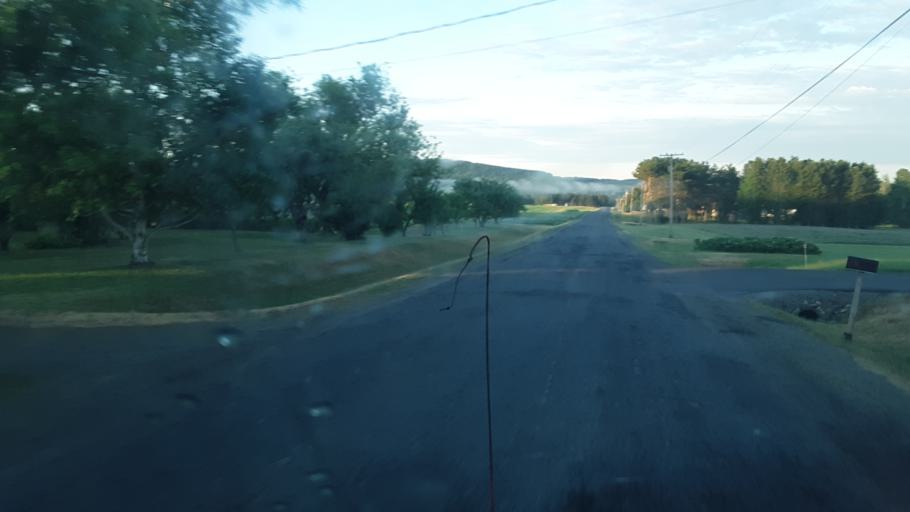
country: US
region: Maine
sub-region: Aroostook County
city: Presque Isle
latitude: 46.7660
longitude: -68.1021
